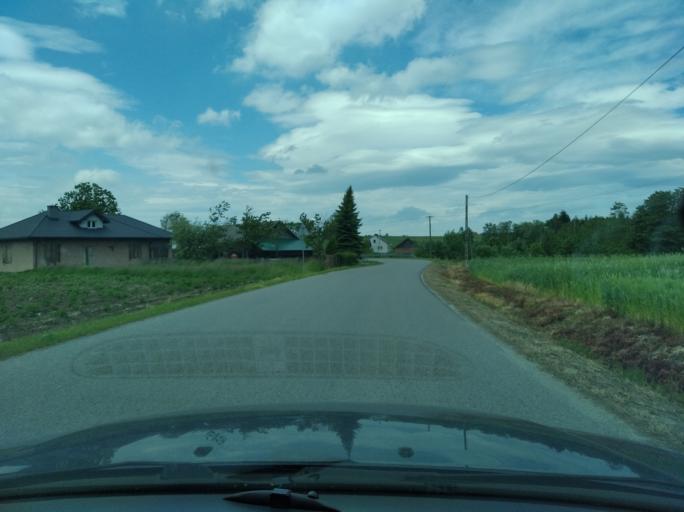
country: PL
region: Subcarpathian Voivodeship
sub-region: Powiat ropczycko-sedziszowski
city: Wielopole Skrzynskie
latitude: 49.9908
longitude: 21.6146
